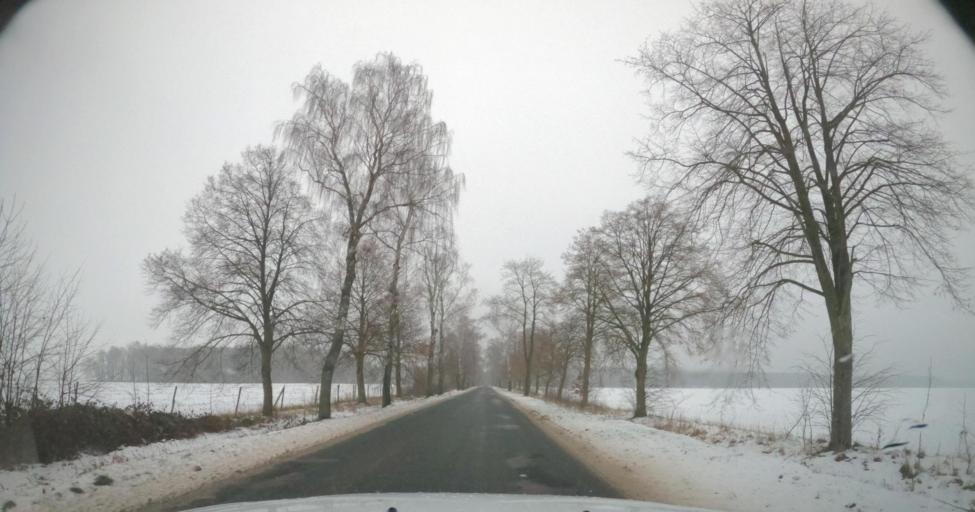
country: PL
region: West Pomeranian Voivodeship
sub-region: Powiat gryficki
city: Gryfice
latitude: 53.9085
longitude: 15.2497
